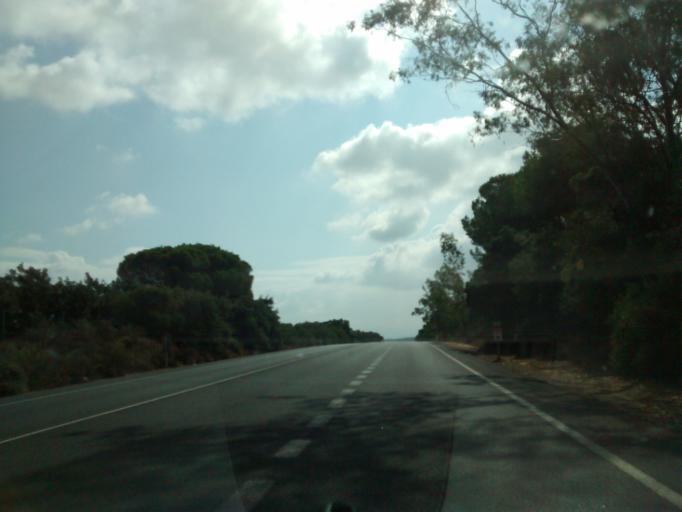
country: ES
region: Andalusia
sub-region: Provincia de Cadiz
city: Vejer de la Frontera
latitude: 36.2547
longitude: -5.9422
